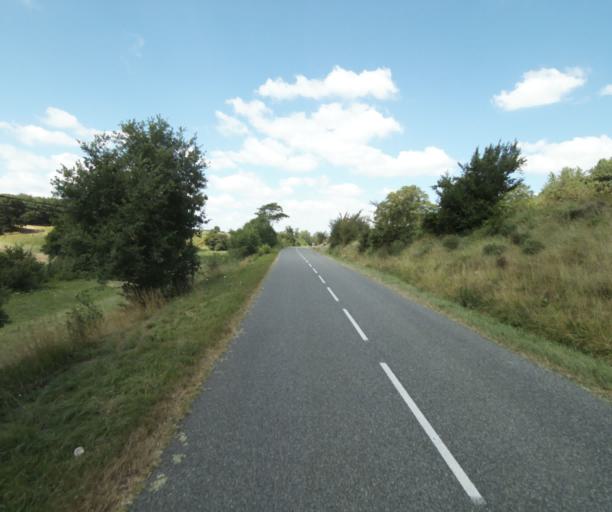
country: FR
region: Midi-Pyrenees
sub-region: Departement de la Haute-Garonne
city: Auriac-sur-Vendinelle
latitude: 43.4782
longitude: 1.8055
